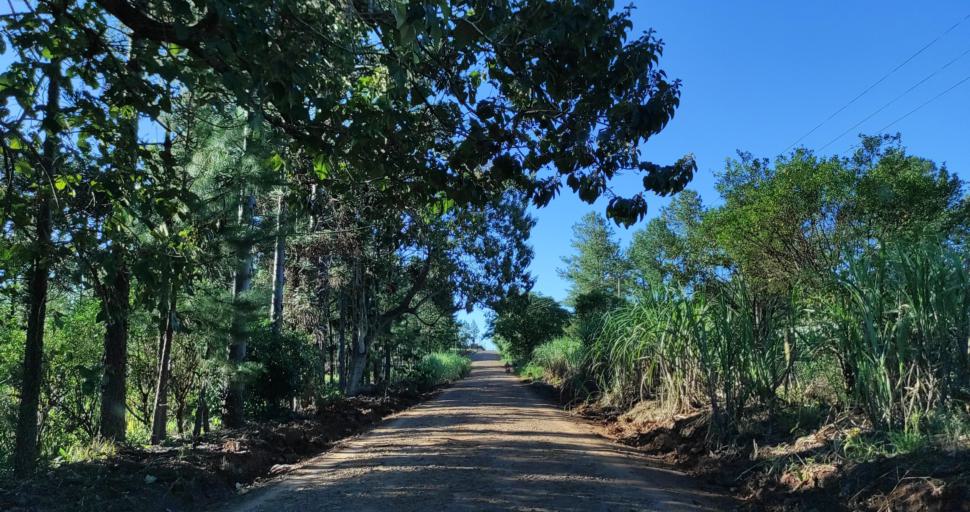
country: AR
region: Misiones
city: Puerto Rico
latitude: -26.8267
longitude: -55.0011
